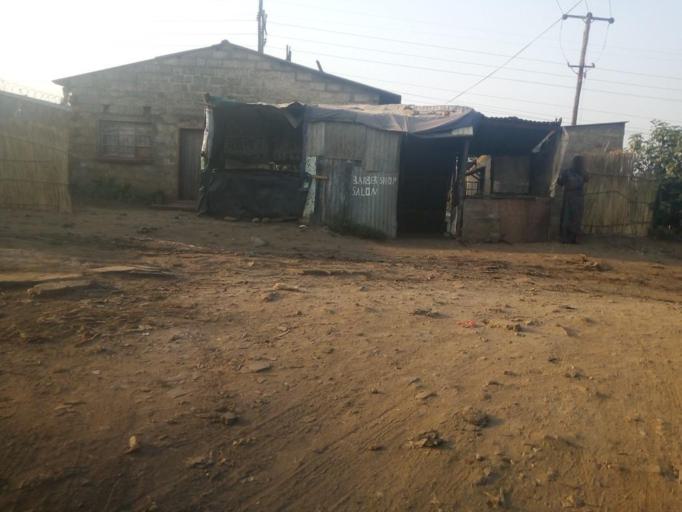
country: ZM
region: Lusaka
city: Lusaka
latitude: -15.4098
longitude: 28.3639
